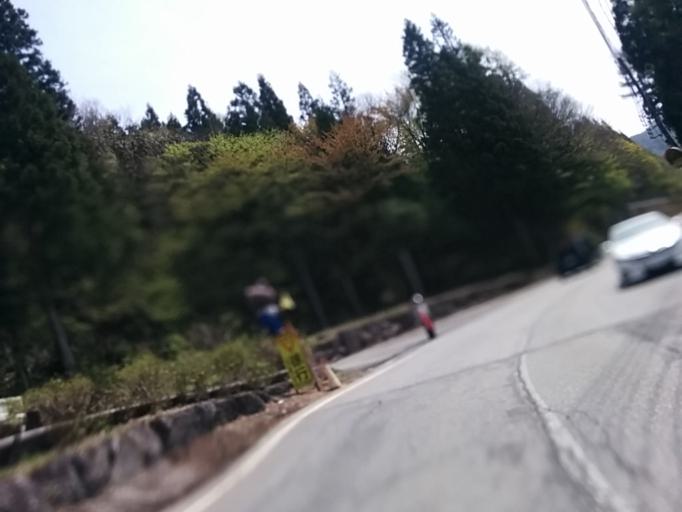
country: JP
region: Gifu
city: Takayama
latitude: 36.2165
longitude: 137.5437
